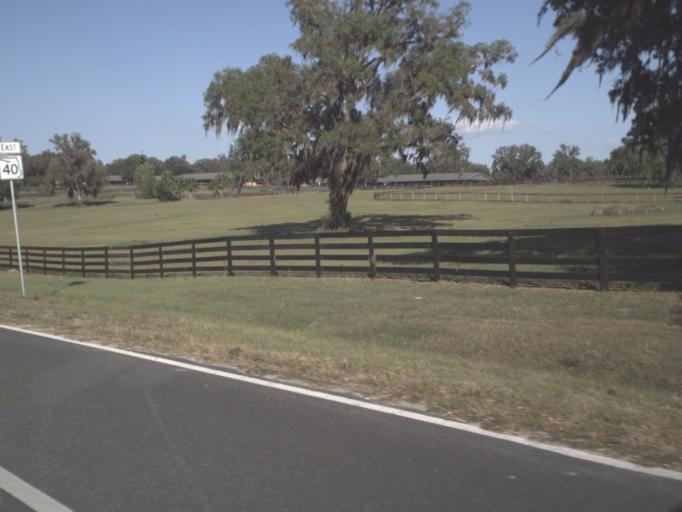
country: US
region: Florida
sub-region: Marion County
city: Dunnellon
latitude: 29.1586
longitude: -82.3511
